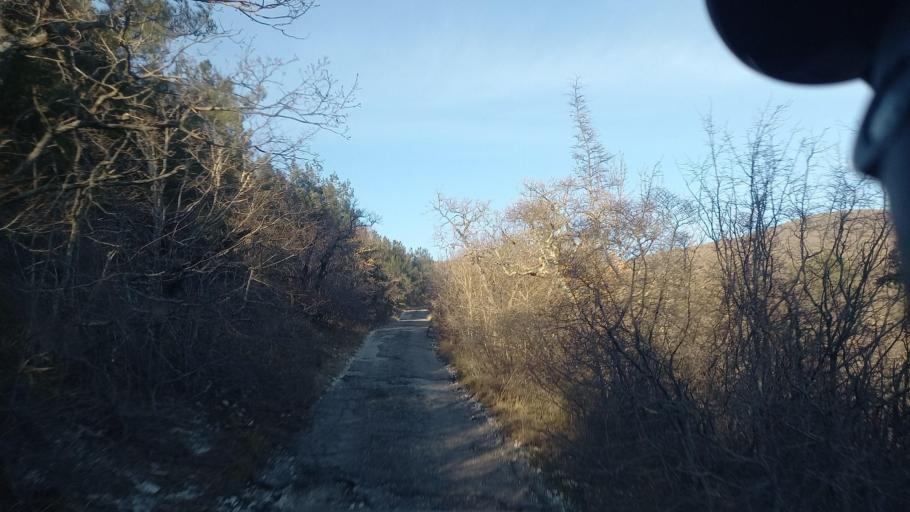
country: RU
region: Krasnodarskiy
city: Kabardinka
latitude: 44.6118
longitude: 37.9411
